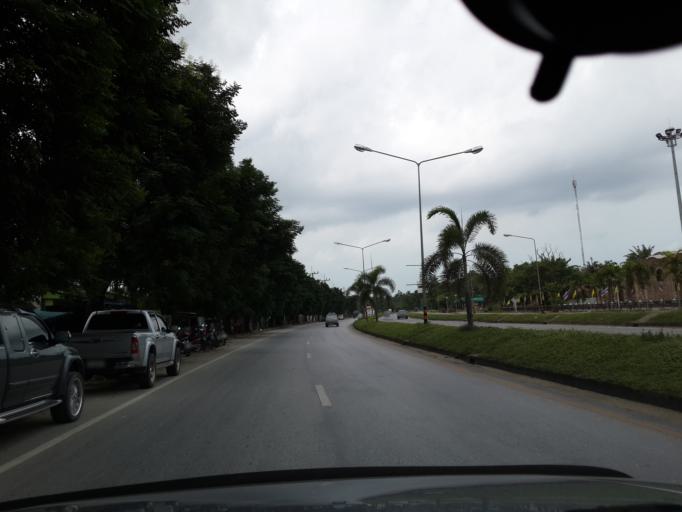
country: TH
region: Pattani
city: Pattani
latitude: 6.8724
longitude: 101.3035
